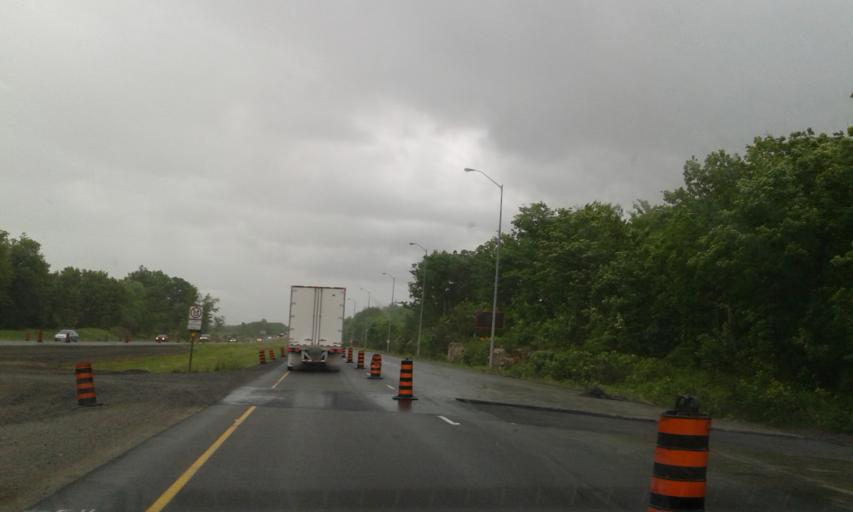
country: CA
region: Ontario
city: Gananoque
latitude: 44.3631
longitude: -76.0752
